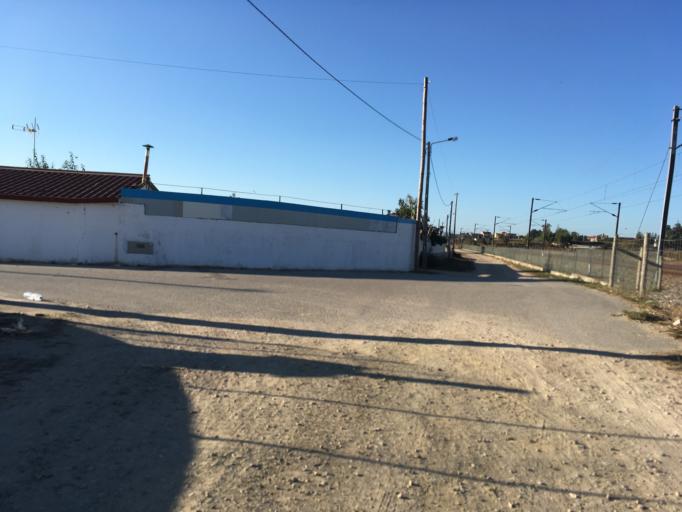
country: PT
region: Aveiro
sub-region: Estarreja
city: Salreu
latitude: 40.7330
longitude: -8.5663
